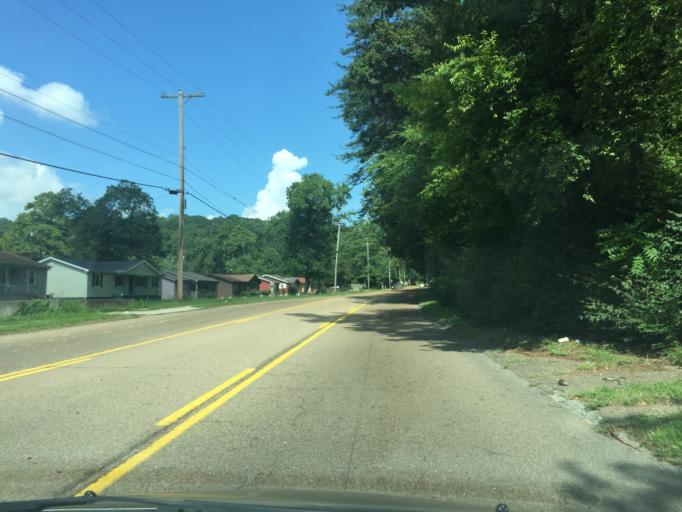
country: US
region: Tennessee
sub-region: Hamilton County
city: East Chattanooga
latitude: 35.0442
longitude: -85.2299
